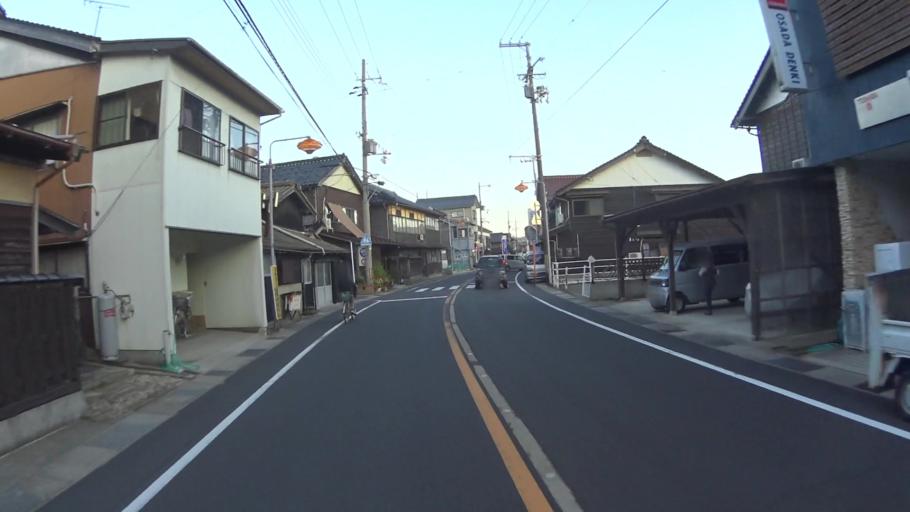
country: JP
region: Kyoto
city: Miyazu
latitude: 35.6875
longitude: 135.0219
